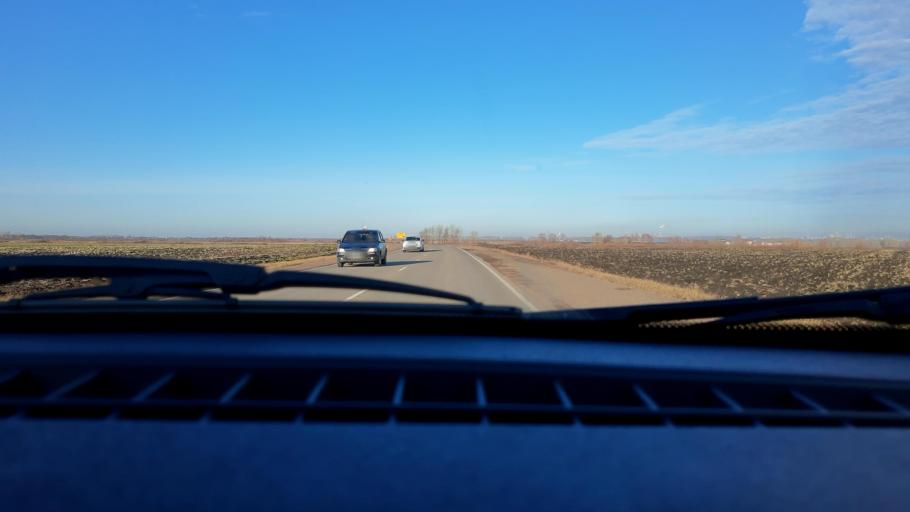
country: RU
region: Bashkortostan
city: Ufa
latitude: 54.8008
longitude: 55.9630
